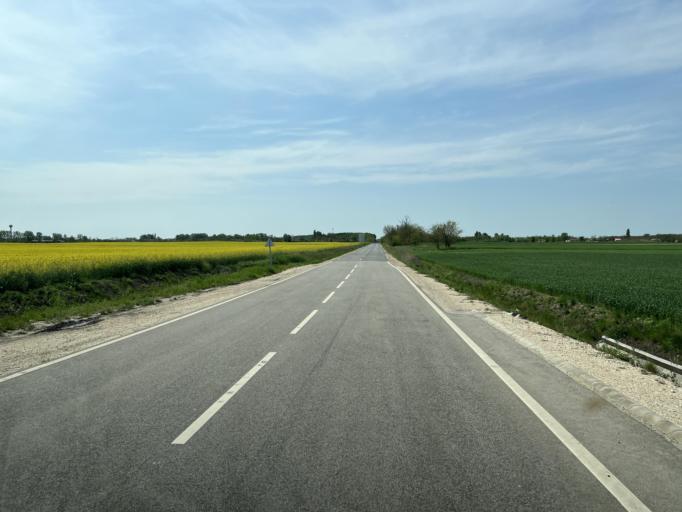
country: HU
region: Pest
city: Abony
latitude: 47.2177
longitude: 20.0166
